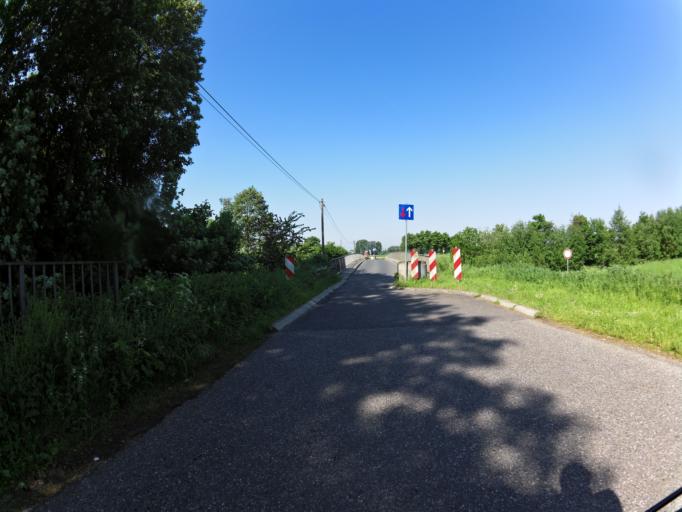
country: DE
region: North Rhine-Westphalia
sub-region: Regierungsbezirk Koln
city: Linnich
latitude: 50.9965
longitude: 6.2732
